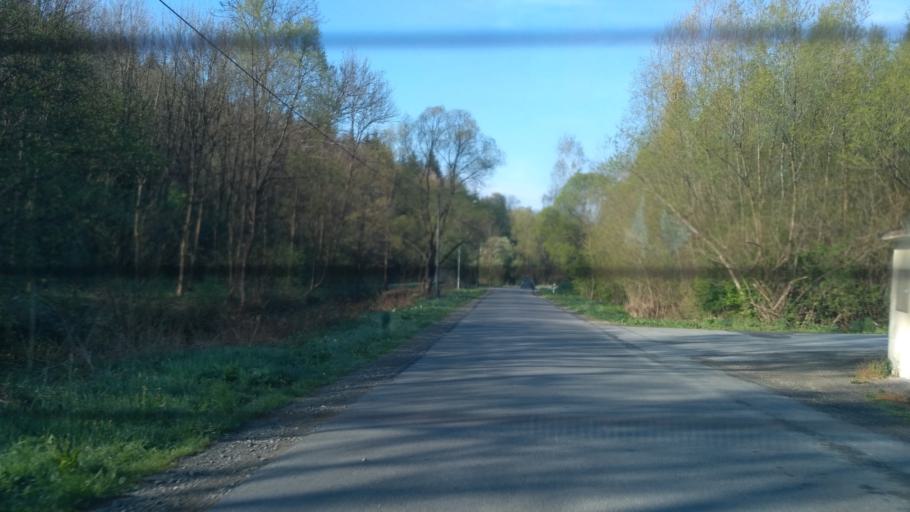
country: PL
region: Subcarpathian Voivodeship
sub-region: Powiat jaroslawski
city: Kramarzowka
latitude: 49.8185
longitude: 22.4944
